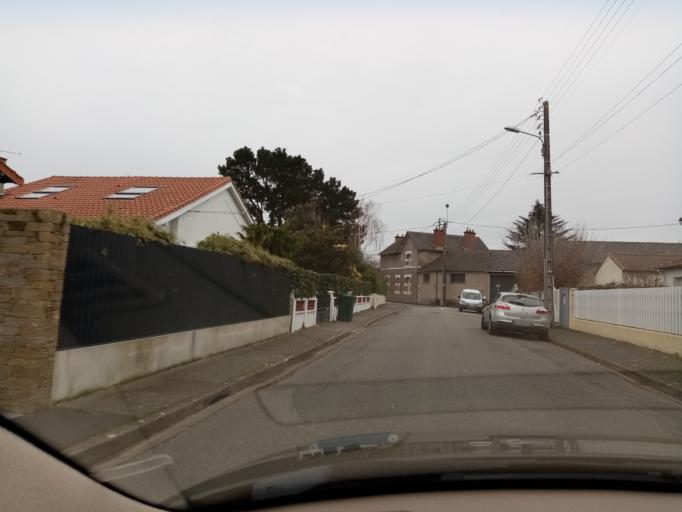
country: FR
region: Pays de la Loire
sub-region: Departement de la Loire-Atlantique
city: Saint-Sebastien-sur-Loire
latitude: 47.2029
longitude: -1.5112
